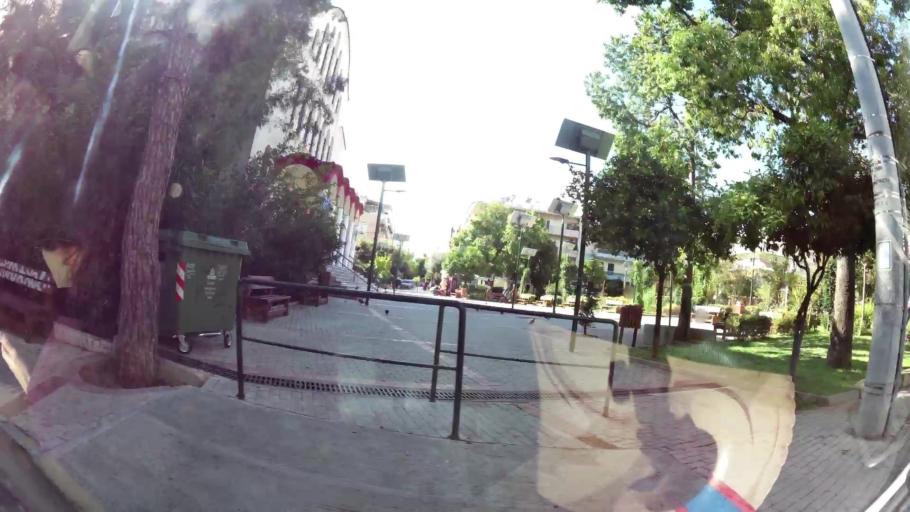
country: GR
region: Attica
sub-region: Nomarchia Athinas
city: Neo Psychiko
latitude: 38.0051
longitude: 23.7836
